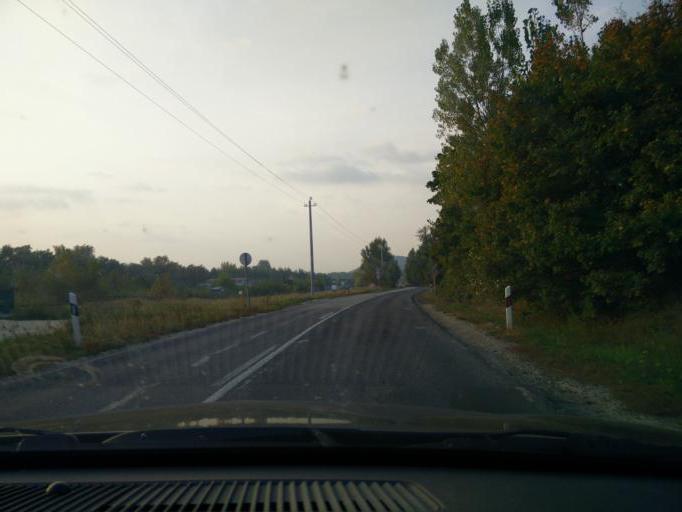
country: HU
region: Pest
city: Piliscsaba
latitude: 47.6424
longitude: 18.8103
